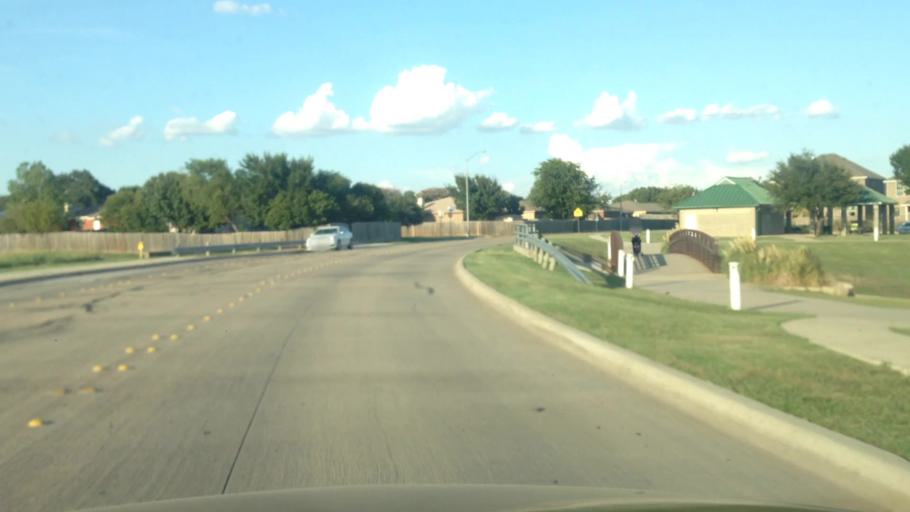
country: US
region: Texas
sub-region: Tarrant County
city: Watauga
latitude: 32.8818
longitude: -97.2581
